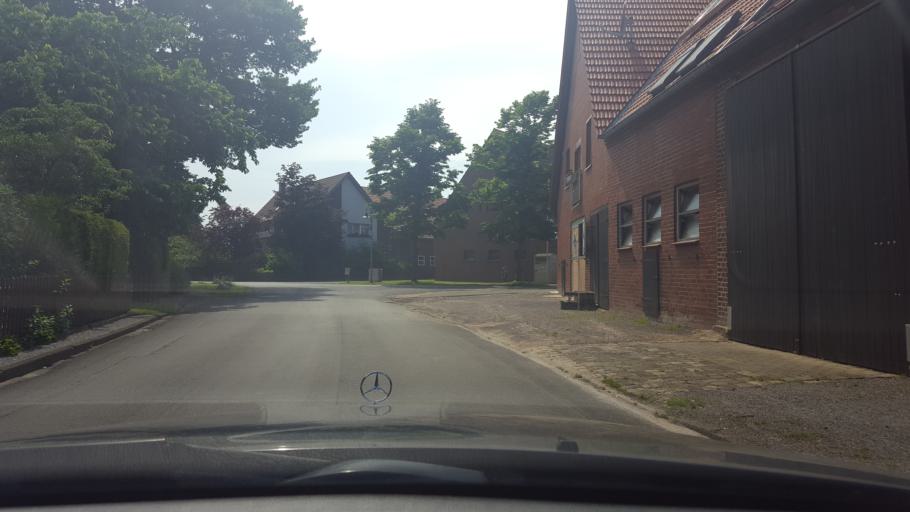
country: DE
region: North Rhine-Westphalia
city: Olfen
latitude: 51.7355
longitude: 7.2897
